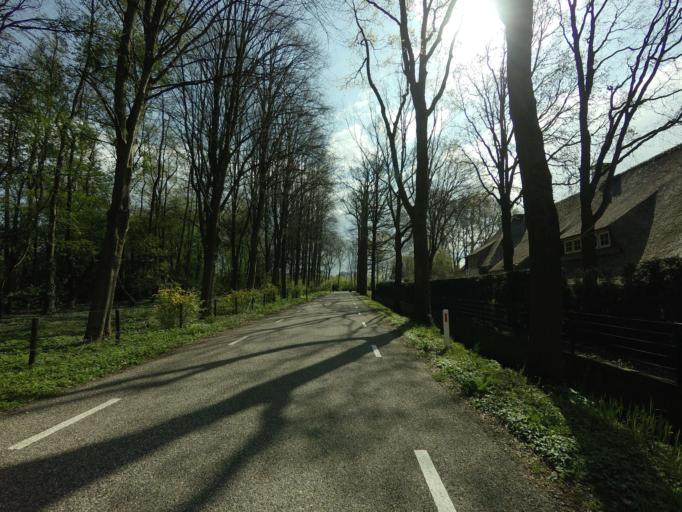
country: NL
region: Utrecht
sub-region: Gemeente Zeist
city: Zeist
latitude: 52.0731
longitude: 5.2274
